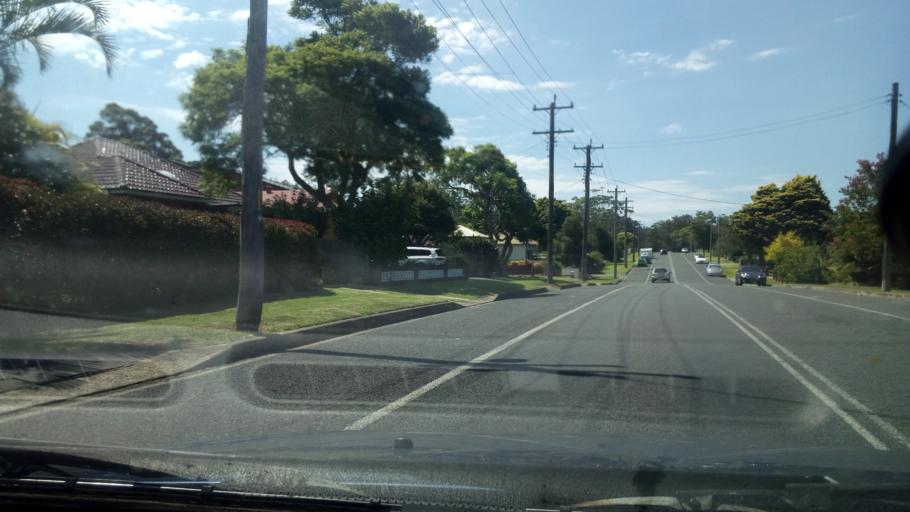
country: AU
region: New South Wales
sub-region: Wollongong
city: Keiraville
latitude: -34.4144
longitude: 150.8750
